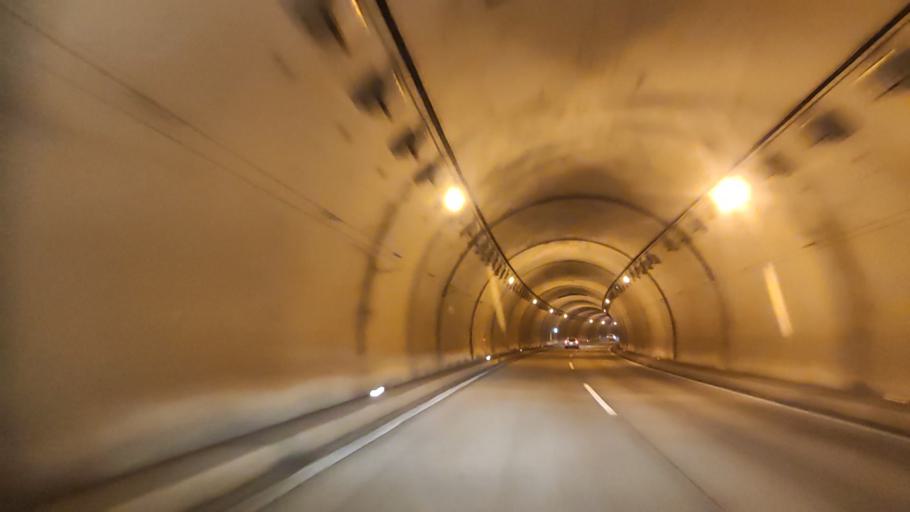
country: JP
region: Ehime
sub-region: Shikoku-chuo Shi
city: Matsuyama
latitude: 33.7911
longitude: 132.9236
